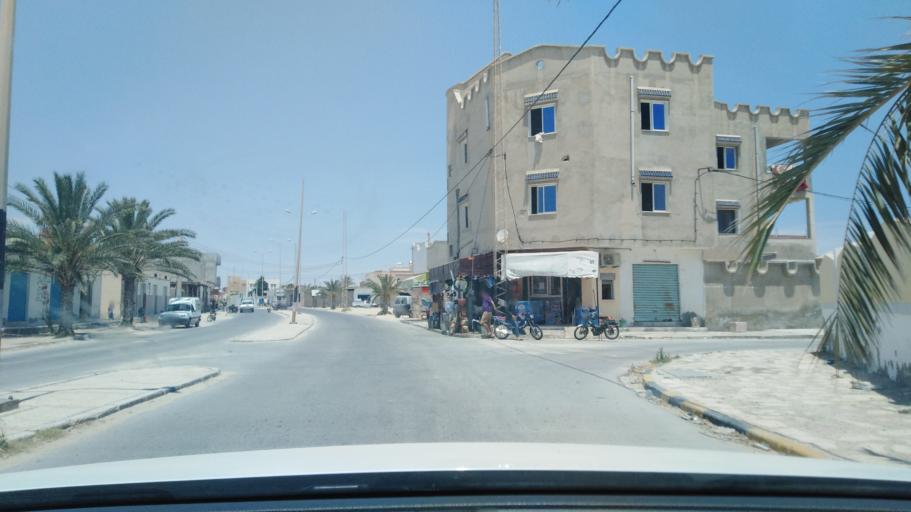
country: TN
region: Qabis
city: Gabes
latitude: 33.9500
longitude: 10.0695
